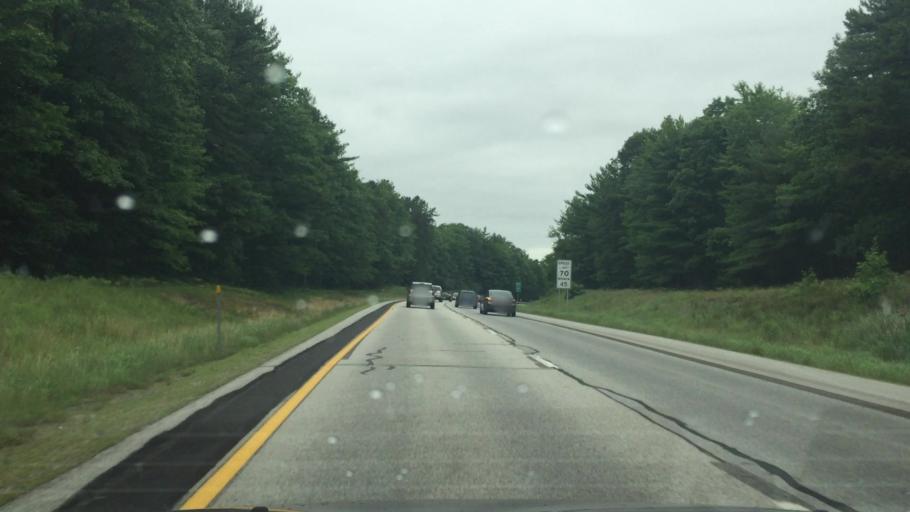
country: US
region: New Hampshire
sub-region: Merrimack County
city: Boscawen
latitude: 43.3395
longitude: -71.6128
